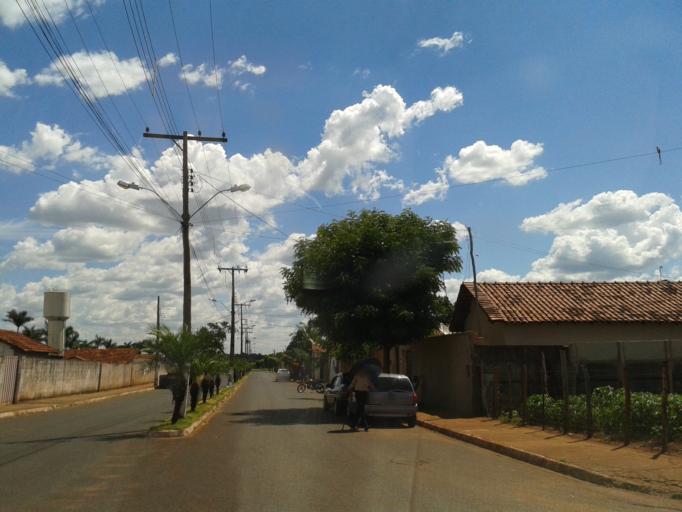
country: BR
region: Minas Gerais
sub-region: Centralina
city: Centralina
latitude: -18.7255
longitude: -49.1939
